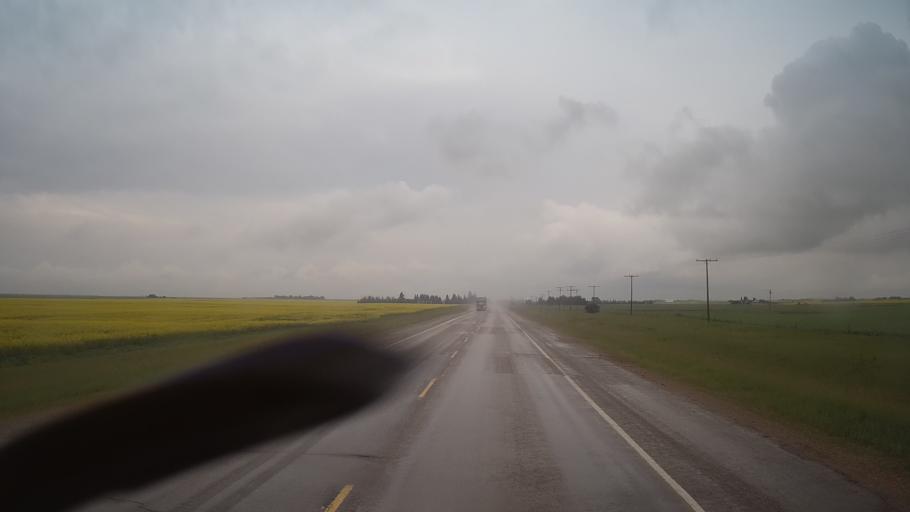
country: CA
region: Saskatchewan
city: Unity
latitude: 52.4349
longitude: -109.0201
